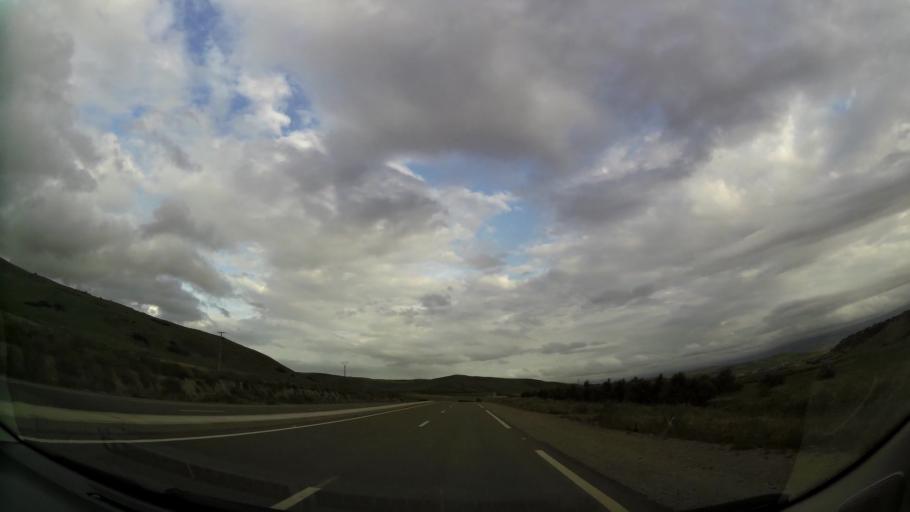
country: MA
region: Taza-Al Hoceima-Taounate
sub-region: Taza
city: Taza
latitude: 34.2858
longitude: -3.9606
